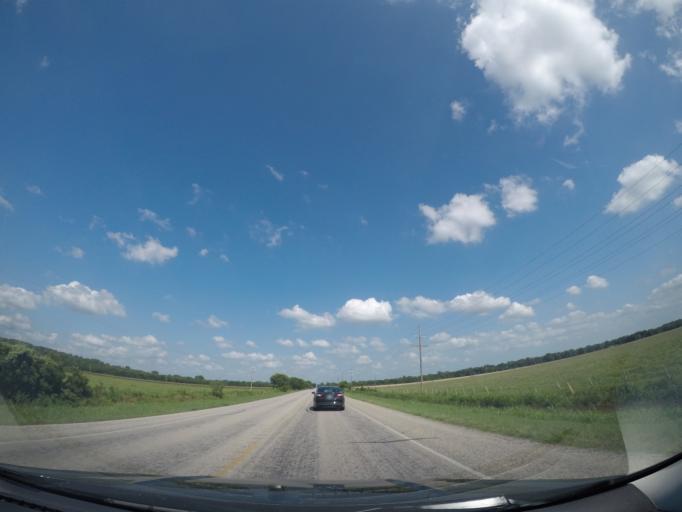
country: US
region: Texas
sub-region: Gonzales County
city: Gonzales
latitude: 29.5033
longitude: -97.5951
